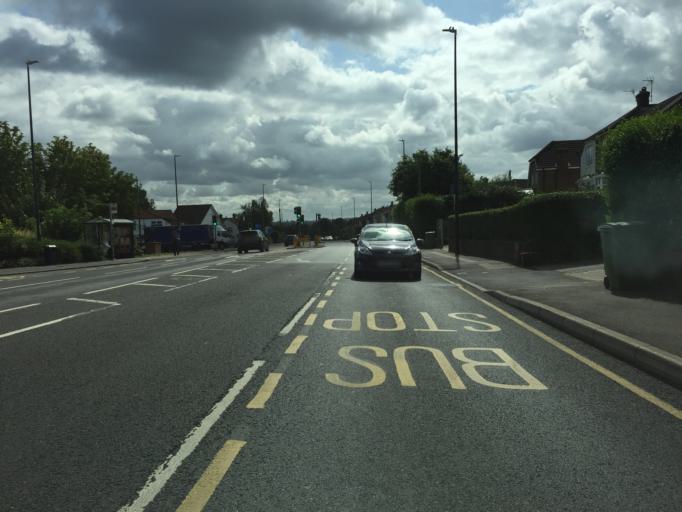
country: GB
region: England
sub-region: Kent
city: Maidstone
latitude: 51.2829
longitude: 0.5005
